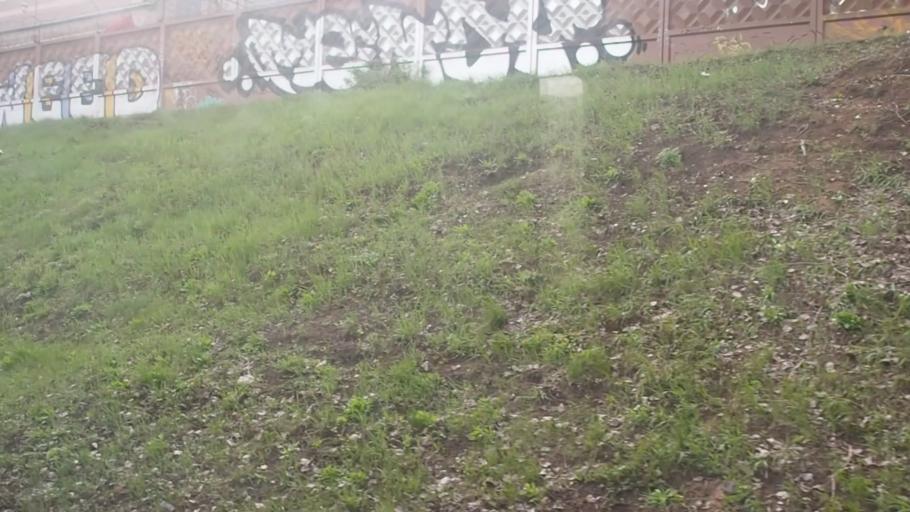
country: RU
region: Moskovskaya
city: Presnenskiy
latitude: 55.7683
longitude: 37.5364
